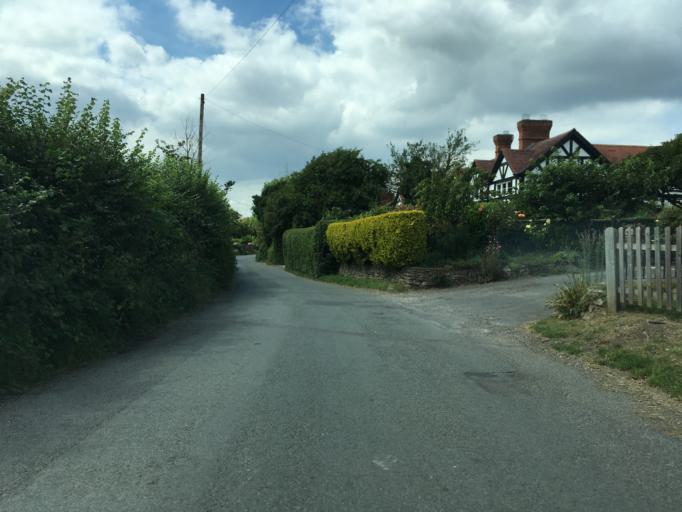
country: GB
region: England
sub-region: Gloucestershire
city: Gloucester
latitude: 51.9083
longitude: -2.2281
